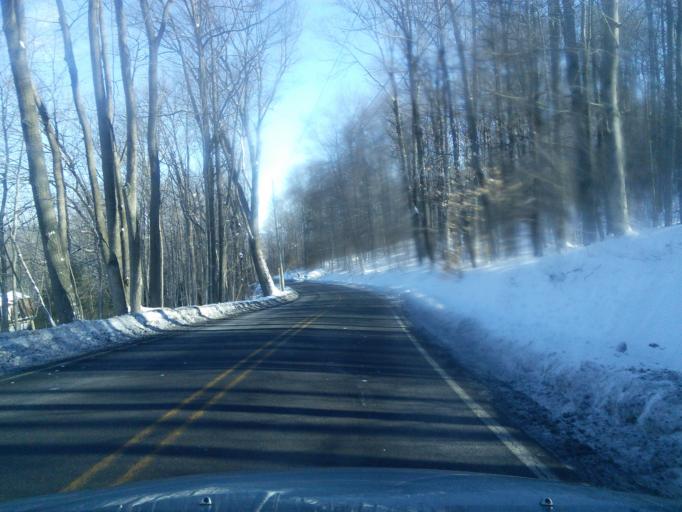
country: US
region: Pennsylvania
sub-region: Centre County
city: Park Forest Village
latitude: 40.8569
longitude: -77.9361
